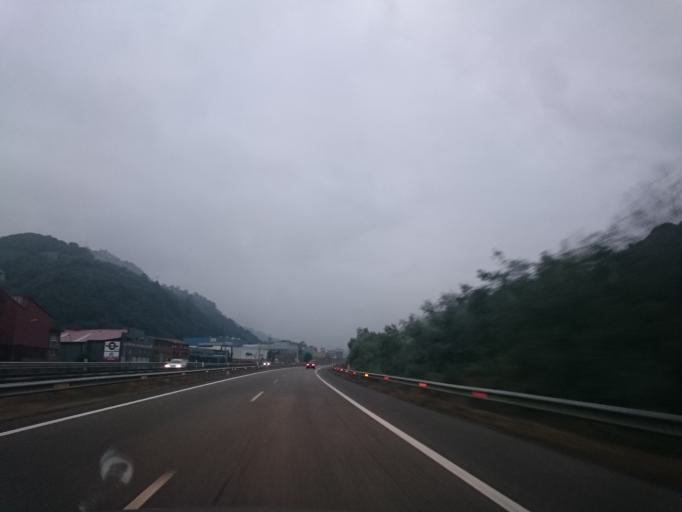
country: ES
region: Asturias
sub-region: Province of Asturias
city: Mieres
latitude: 43.2343
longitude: -5.7806
